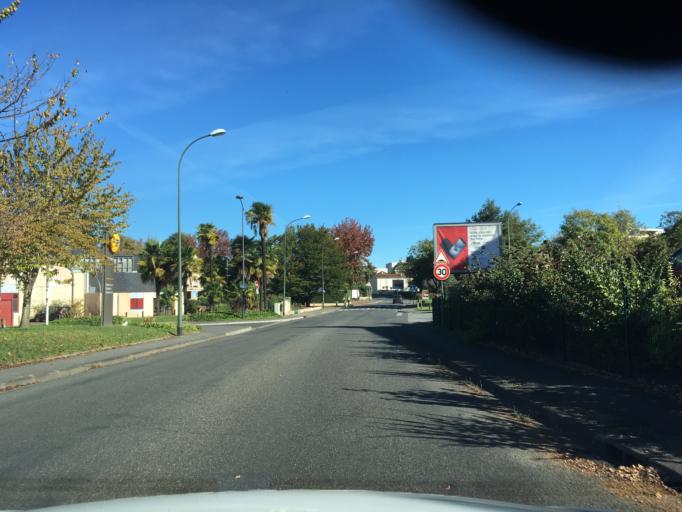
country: FR
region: Aquitaine
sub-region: Departement des Pyrenees-Atlantiques
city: Pau
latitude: 43.3143
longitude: -0.3549
